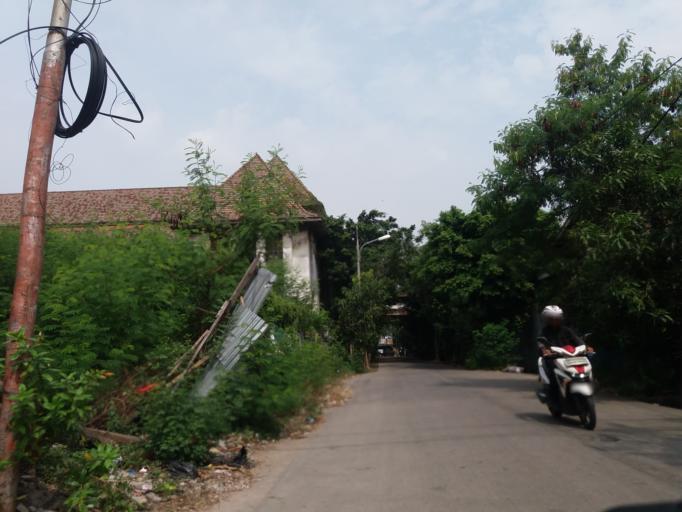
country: ID
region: Jakarta Raya
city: Jakarta
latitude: -6.1321
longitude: 106.8145
